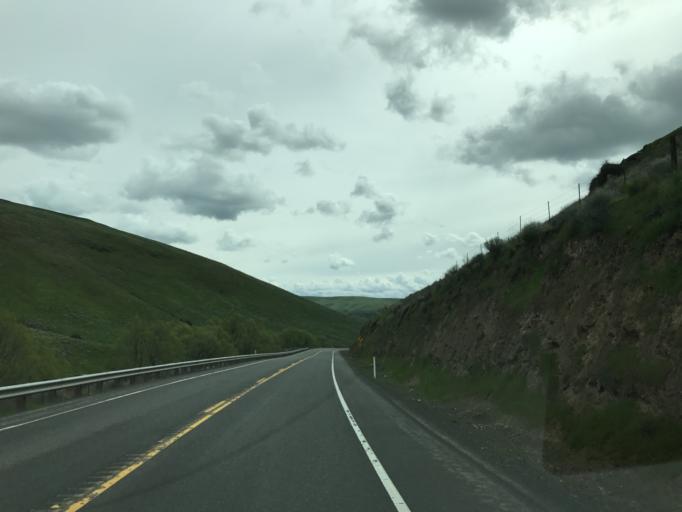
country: US
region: Washington
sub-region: Garfield County
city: Pomeroy
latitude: 46.6526
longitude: -117.8065
